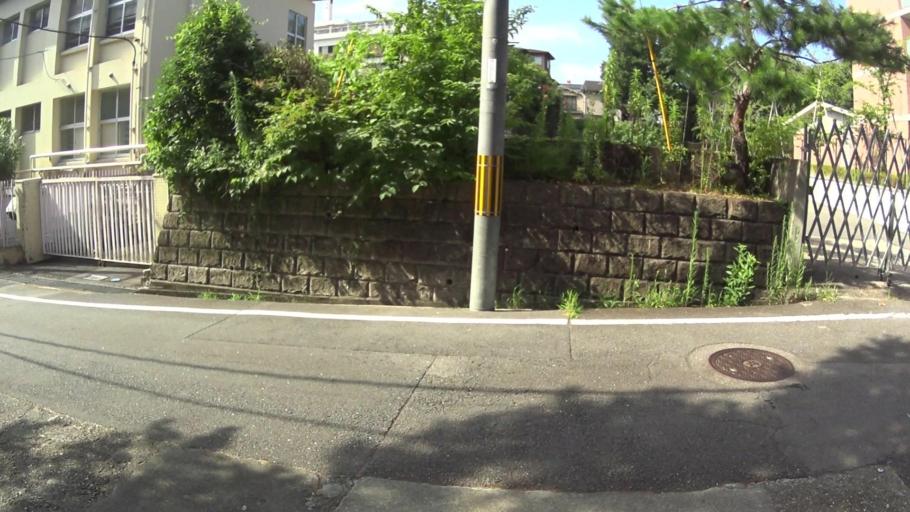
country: RU
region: Rostov
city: Remontnoye
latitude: 46.5015
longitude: 43.7570
